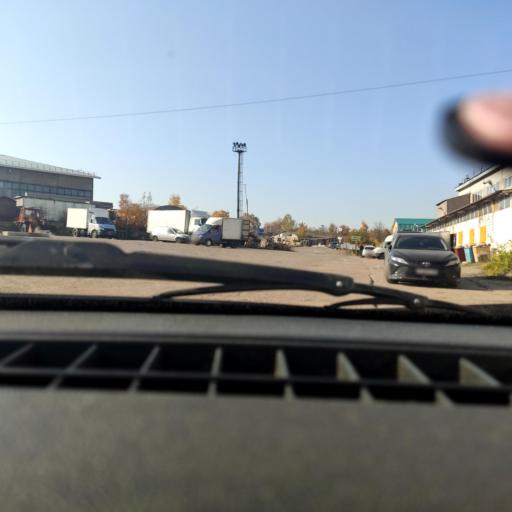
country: RU
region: Bashkortostan
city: Ufa
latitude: 54.8261
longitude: 56.1109
